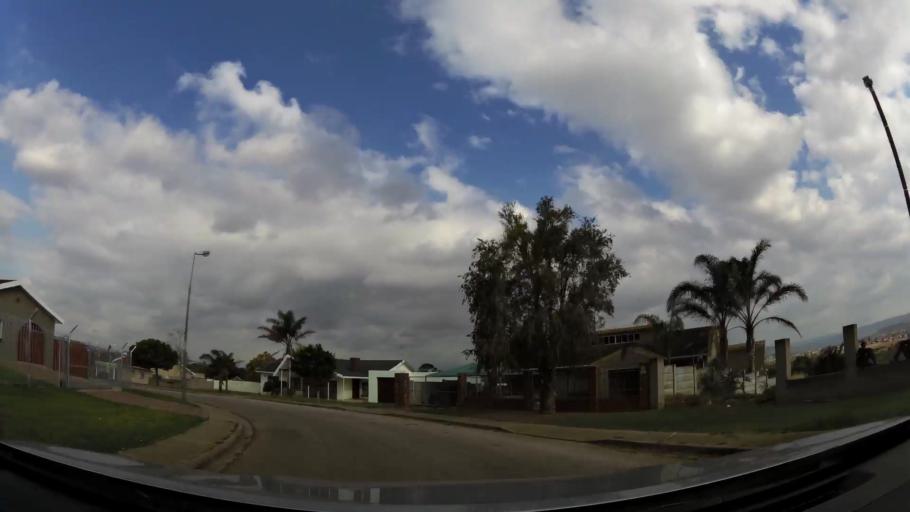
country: ZA
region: Eastern Cape
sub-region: Nelson Mandela Bay Metropolitan Municipality
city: Uitenhage
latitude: -33.7344
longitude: 25.4061
